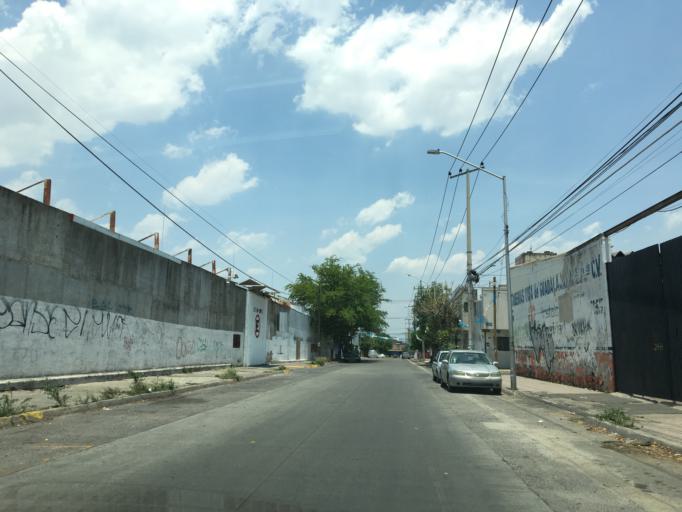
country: MX
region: Jalisco
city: Guadalajara
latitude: 20.6576
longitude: -103.3654
